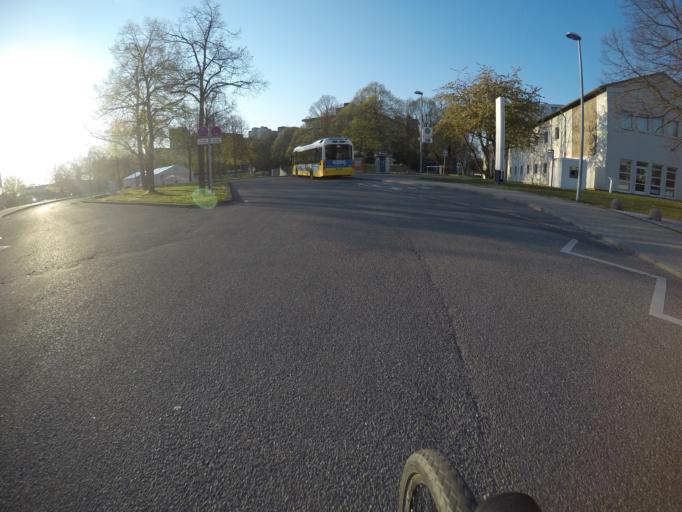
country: DE
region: Baden-Wuerttemberg
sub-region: Regierungsbezirk Stuttgart
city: Gerlingen
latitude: 48.7456
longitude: 9.1075
